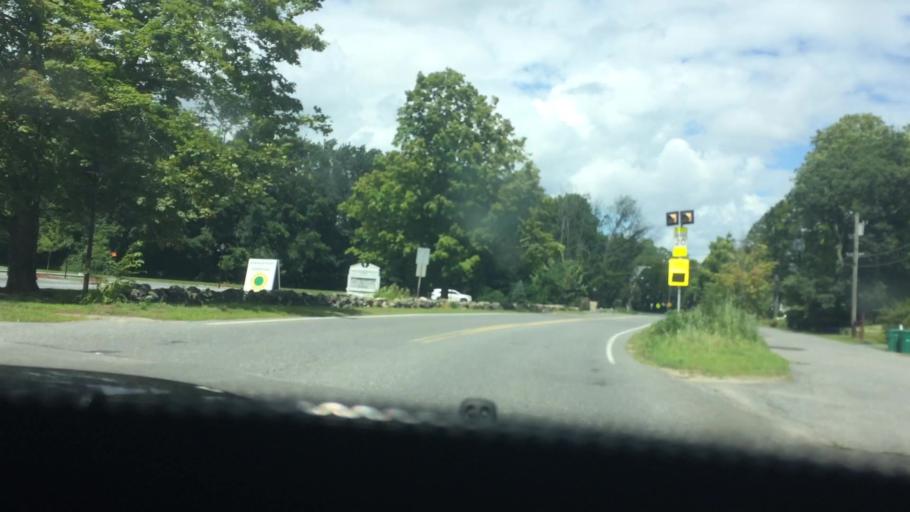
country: US
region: Massachusetts
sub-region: Middlesex County
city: Sudbury
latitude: 42.3803
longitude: -71.4087
